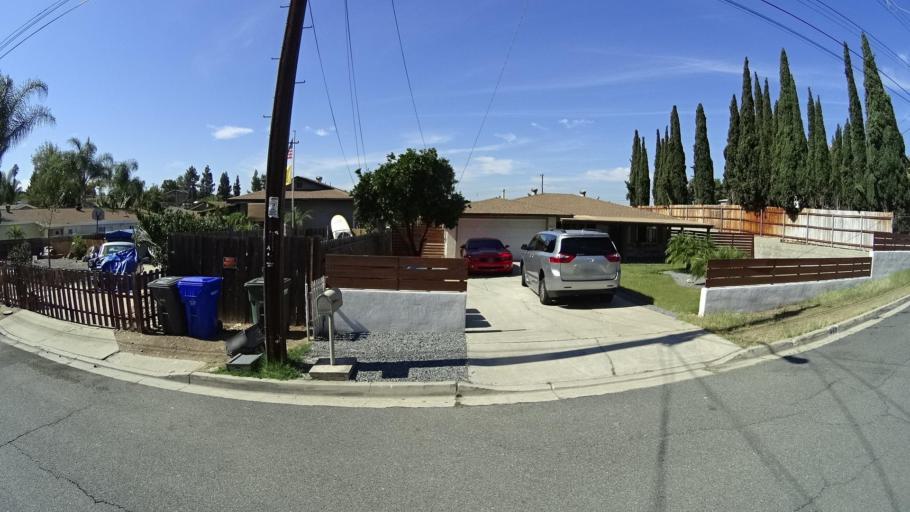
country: US
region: California
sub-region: San Diego County
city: La Presa
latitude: 32.7056
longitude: -117.0001
